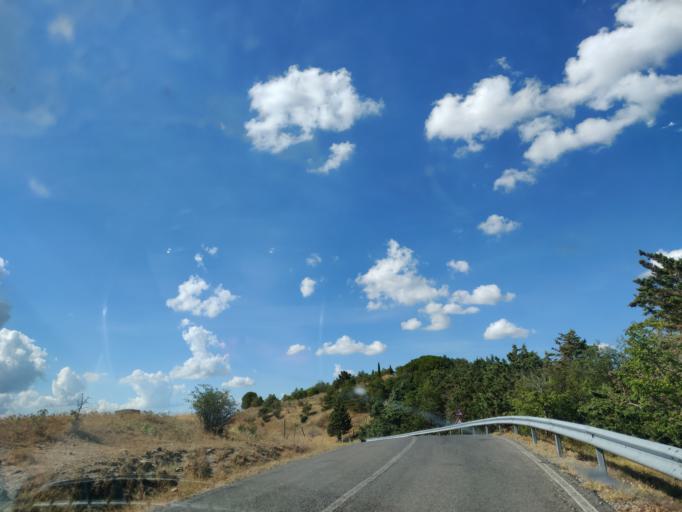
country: IT
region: Tuscany
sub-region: Provincia di Siena
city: Radicofani
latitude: 42.9467
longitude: 11.7342
